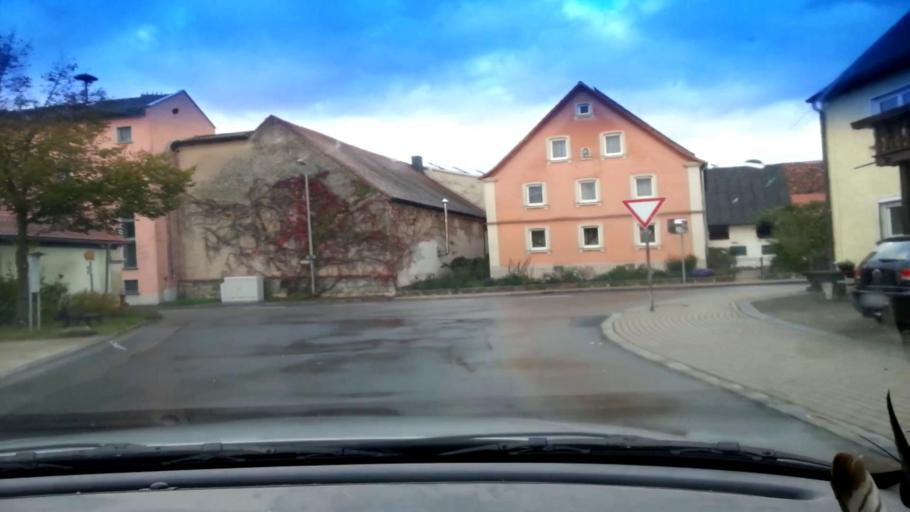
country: DE
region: Bavaria
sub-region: Upper Franconia
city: Burgebrach
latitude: 49.8185
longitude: 10.6774
